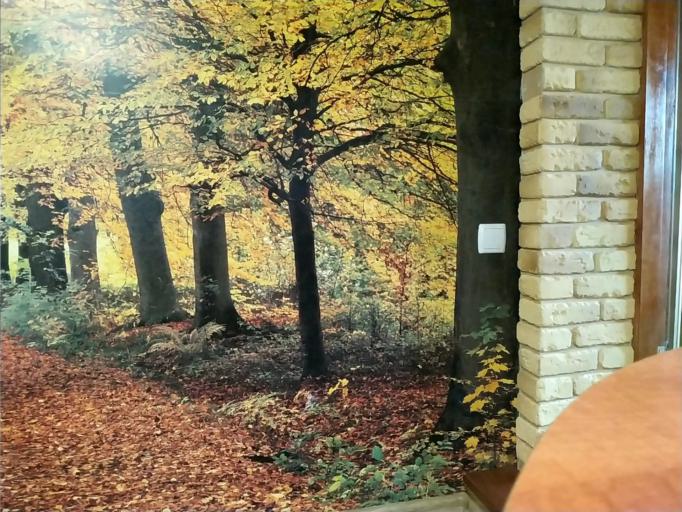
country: RU
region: Leningrad
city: Tolmachevo
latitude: 58.9301
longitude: 29.7196
